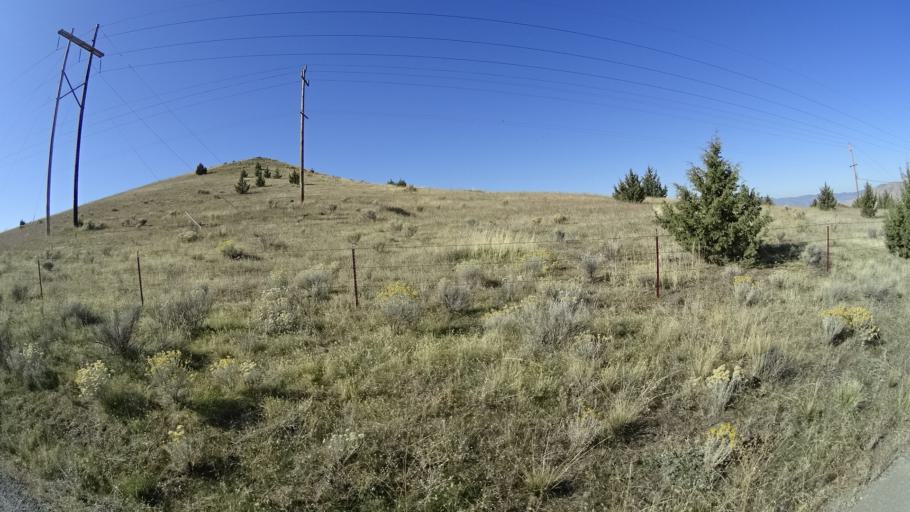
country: US
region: California
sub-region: Siskiyou County
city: Montague
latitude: 41.7745
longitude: -122.3587
